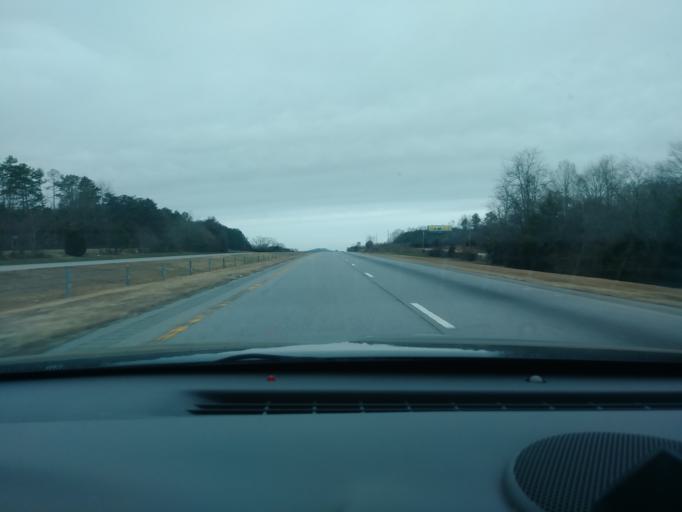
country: US
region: North Carolina
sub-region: Yadkin County
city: Jonesville
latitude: 36.1251
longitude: -80.8245
